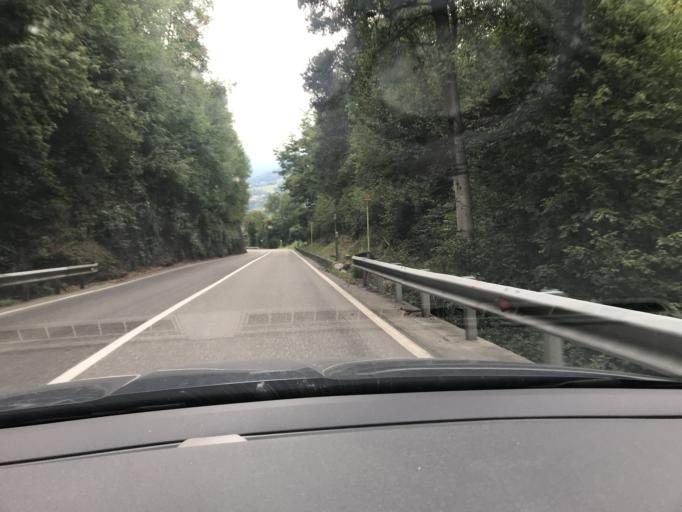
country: IT
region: Trentino-Alto Adige
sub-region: Bolzano
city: Chiusa
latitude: 46.6380
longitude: 11.5709
